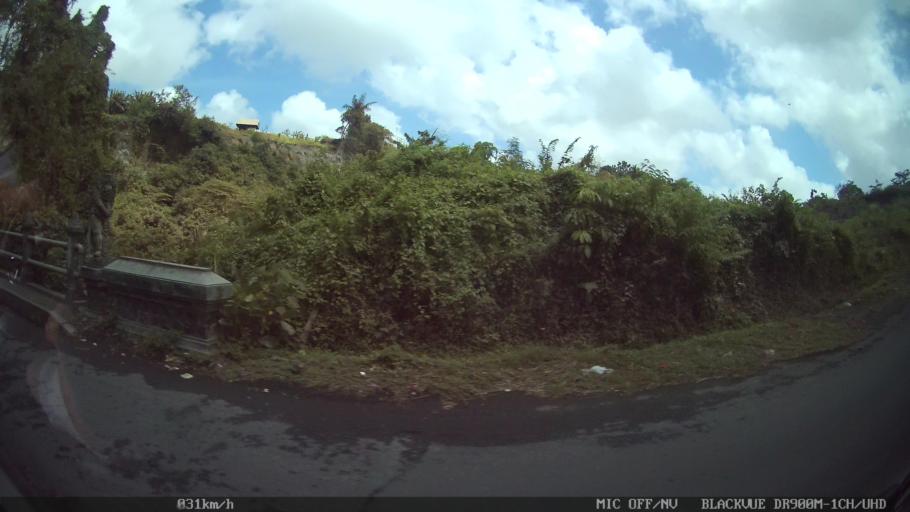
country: ID
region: Bali
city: Banjar Pasekan
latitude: -8.5871
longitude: 115.2879
